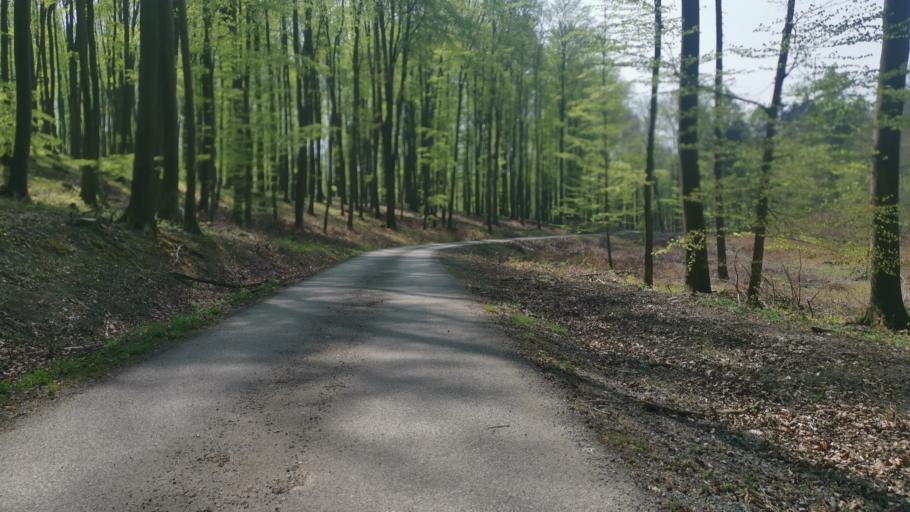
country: SK
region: Nitriansky
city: Brezova pod Bradlom
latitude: 48.5954
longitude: 17.4933
